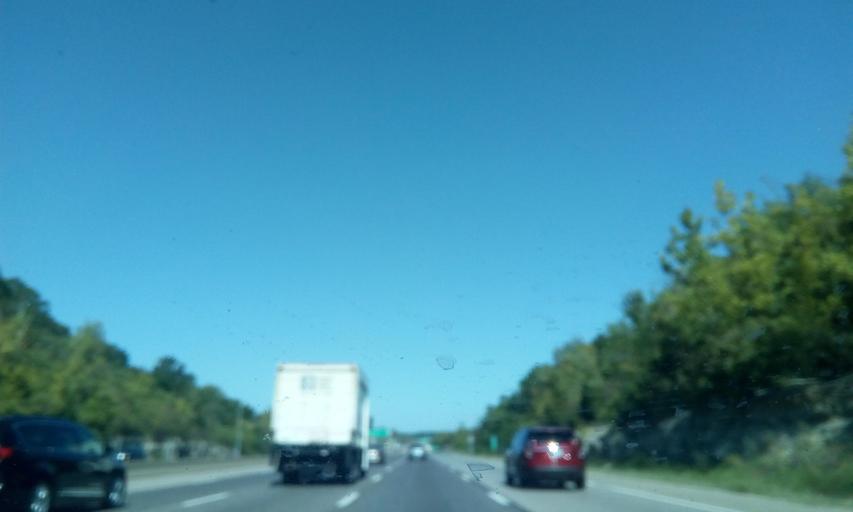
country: US
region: Missouri
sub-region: Saint Louis County
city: Sunset Hills
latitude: 38.5354
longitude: -90.4116
